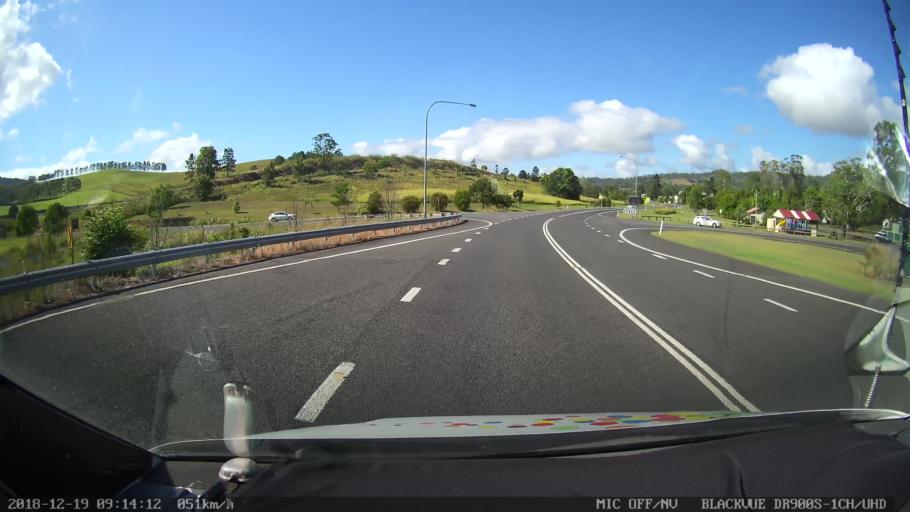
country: AU
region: New South Wales
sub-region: Kyogle
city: Kyogle
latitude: -28.5063
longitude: 152.9674
